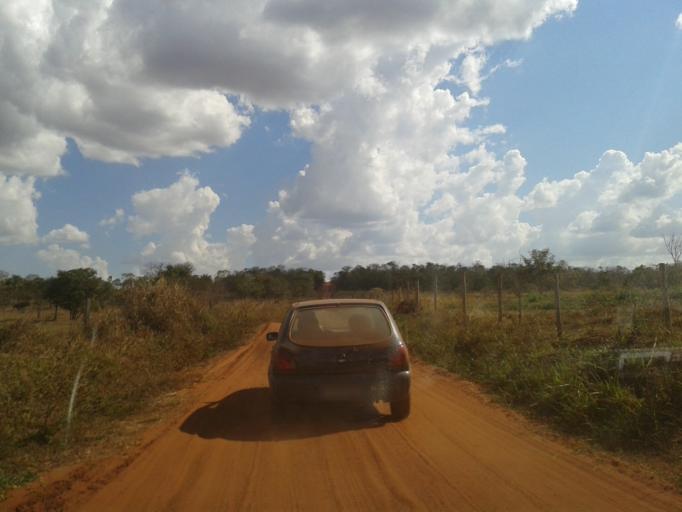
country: BR
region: Minas Gerais
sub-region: Santa Vitoria
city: Santa Vitoria
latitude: -19.1953
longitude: -49.9188
